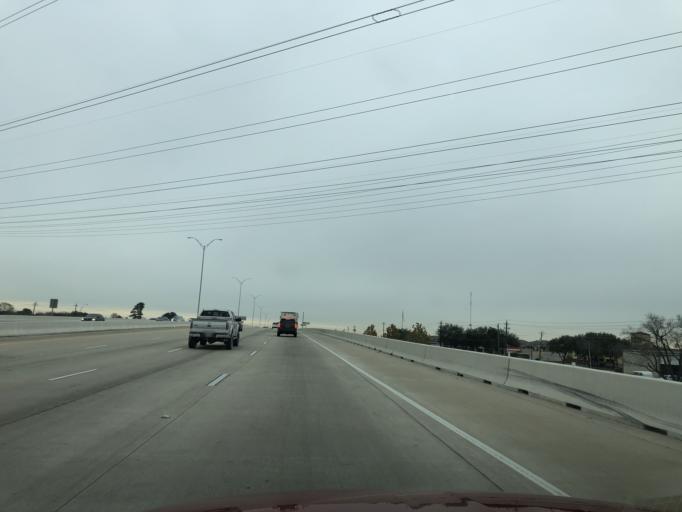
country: US
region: Texas
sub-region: Fort Bend County
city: Missouri City
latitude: 29.6216
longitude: -95.5113
